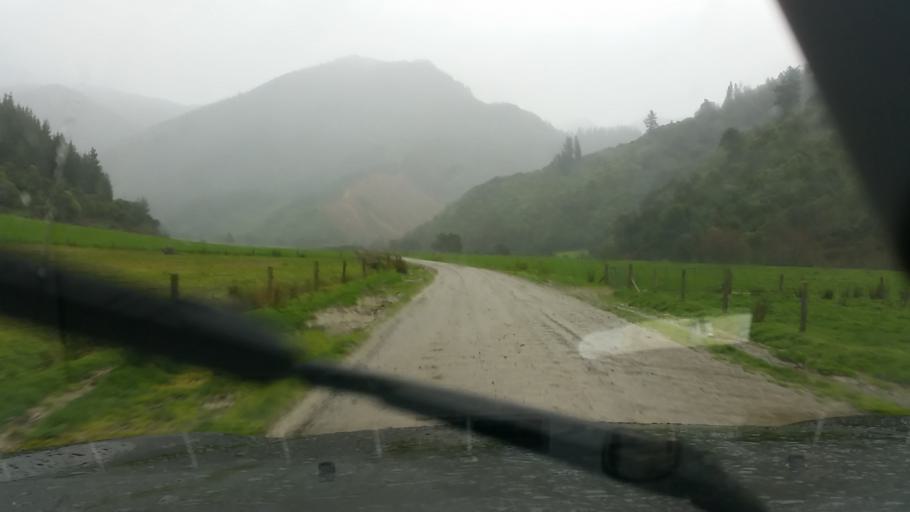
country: NZ
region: Marlborough
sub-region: Marlborough District
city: Picton
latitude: -41.3552
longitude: 173.9266
